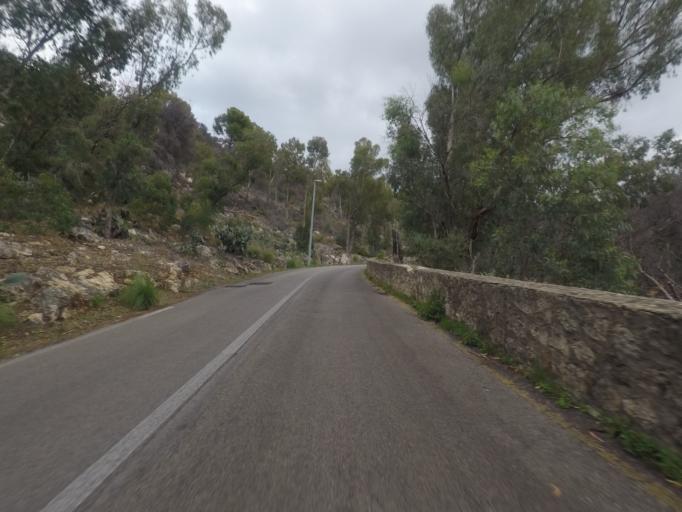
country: IT
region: Sicily
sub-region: Palermo
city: Palermo
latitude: 38.1552
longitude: 13.3607
